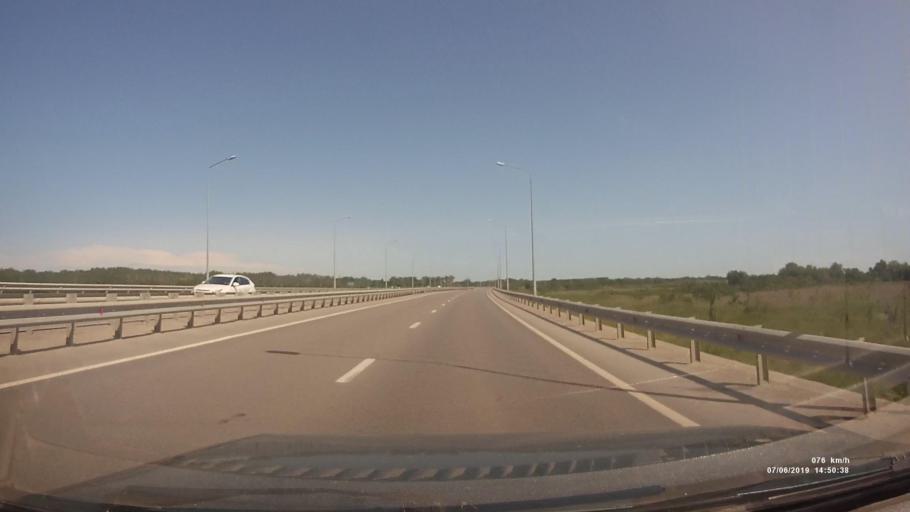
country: RU
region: Rostov
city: Rostov-na-Donu
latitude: 47.2067
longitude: 39.7496
